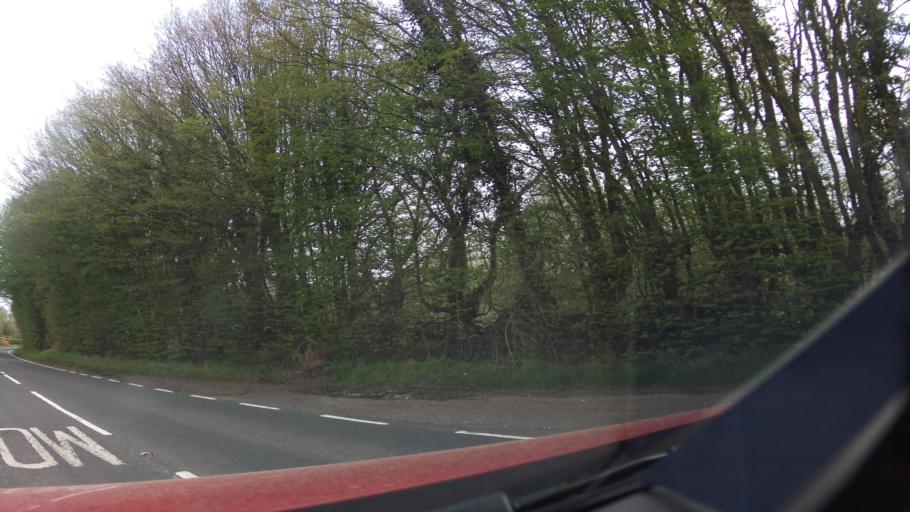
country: GB
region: England
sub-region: Hampshire
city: Chandlers Ford
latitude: 51.0203
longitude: -1.3864
